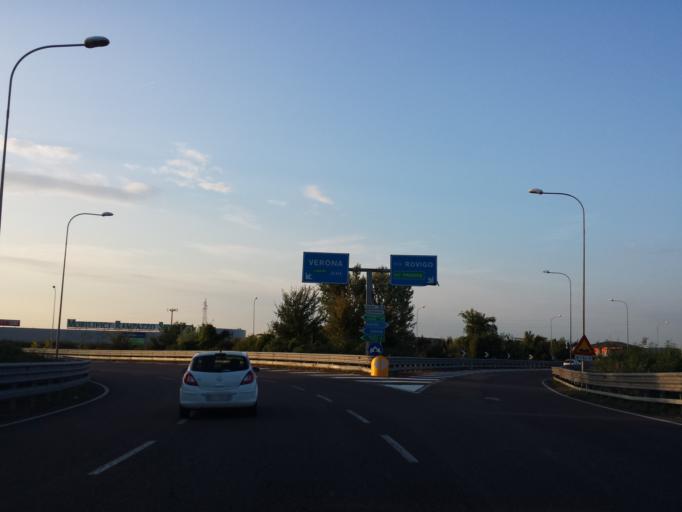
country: IT
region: Veneto
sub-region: Provincia di Rovigo
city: Bosaro
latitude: 45.0277
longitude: 11.7754
